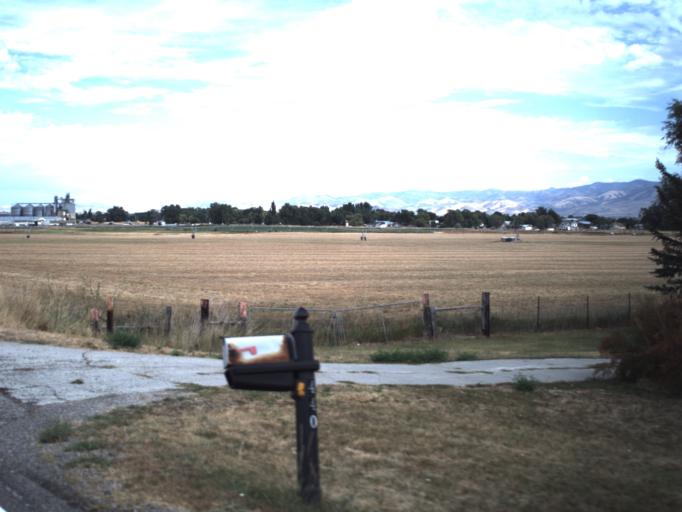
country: US
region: Utah
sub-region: Cache County
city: Lewiston
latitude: 41.9096
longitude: -111.9527
